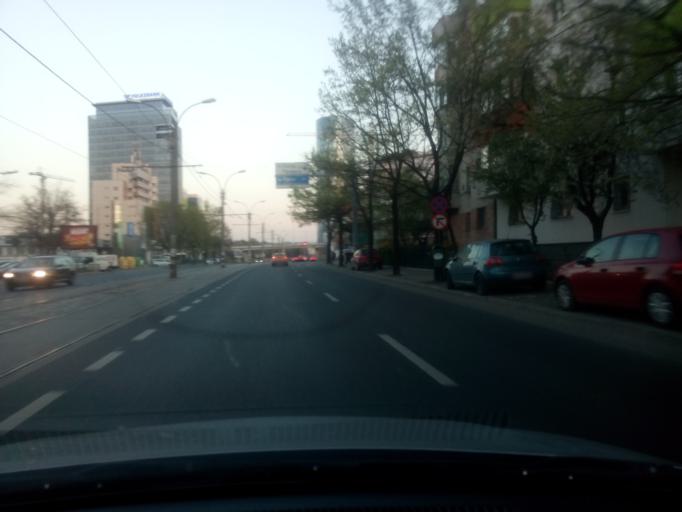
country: RO
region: Bucuresti
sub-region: Municipiul Bucuresti
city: Bucharest
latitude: 44.4818
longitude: 26.1005
